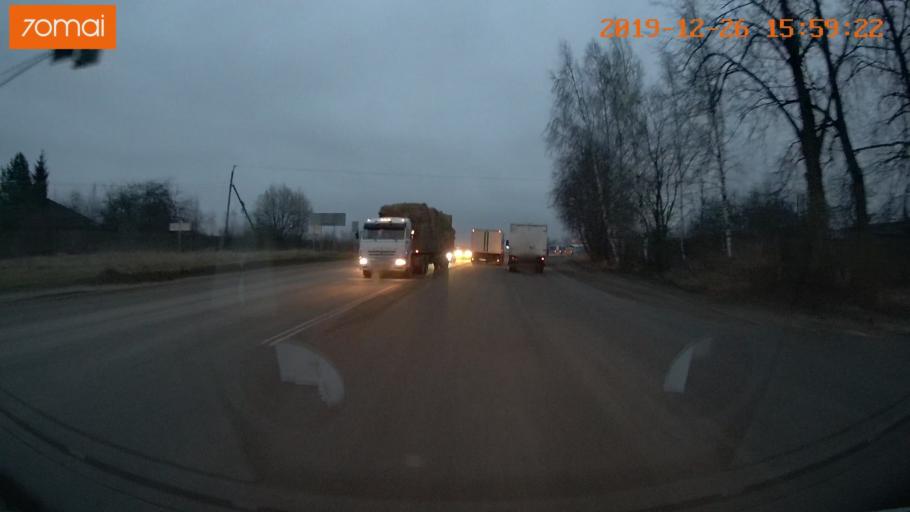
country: RU
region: Jaroslavl
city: Rybinsk
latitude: 58.0321
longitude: 38.8037
